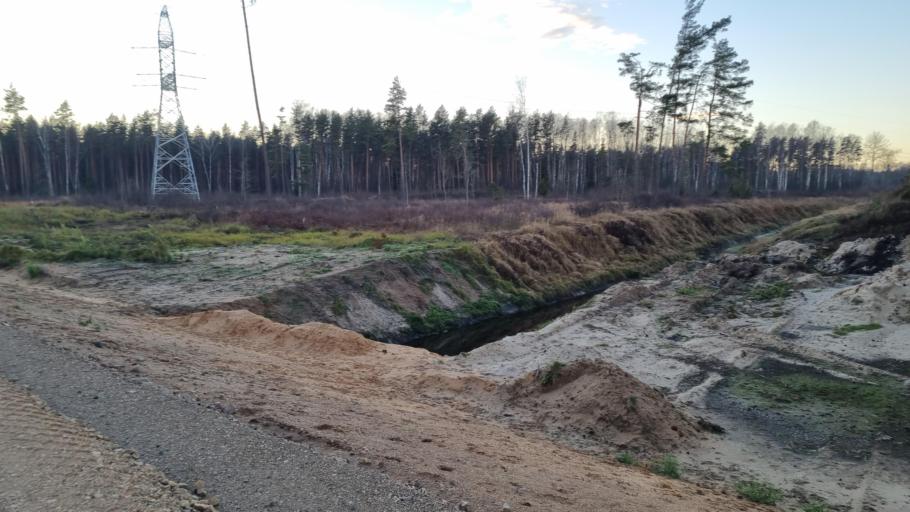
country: LV
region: Kekava
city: Balozi
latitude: 56.8648
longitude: 24.1615
